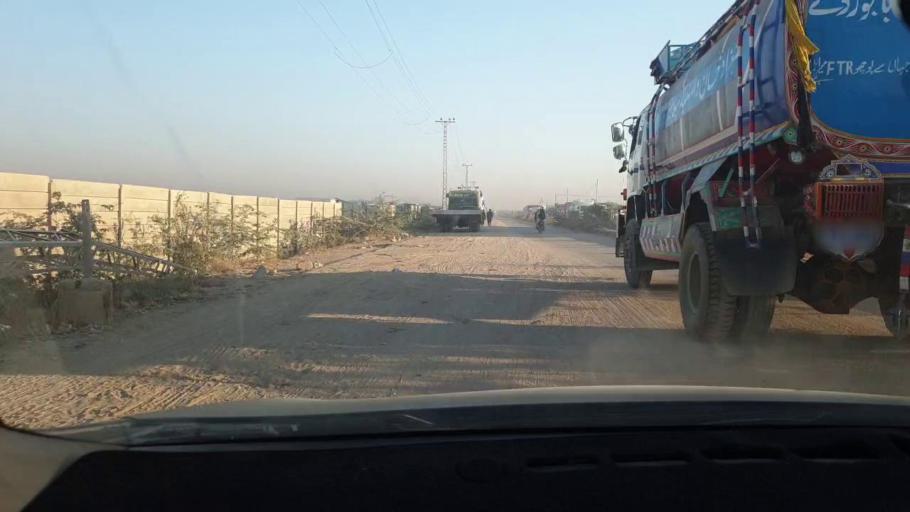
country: PK
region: Sindh
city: Malir Cantonment
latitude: 25.0148
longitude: 67.1703
